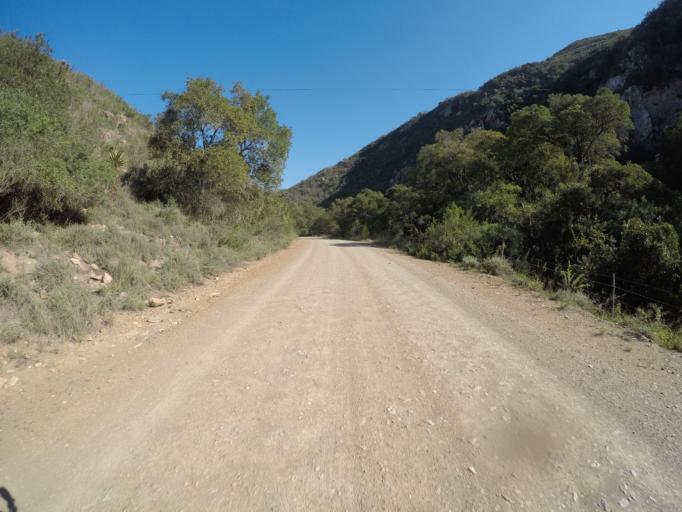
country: ZA
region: Eastern Cape
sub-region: Cacadu District Municipality
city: Kareedouw
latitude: -33.6604
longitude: 24.5395
